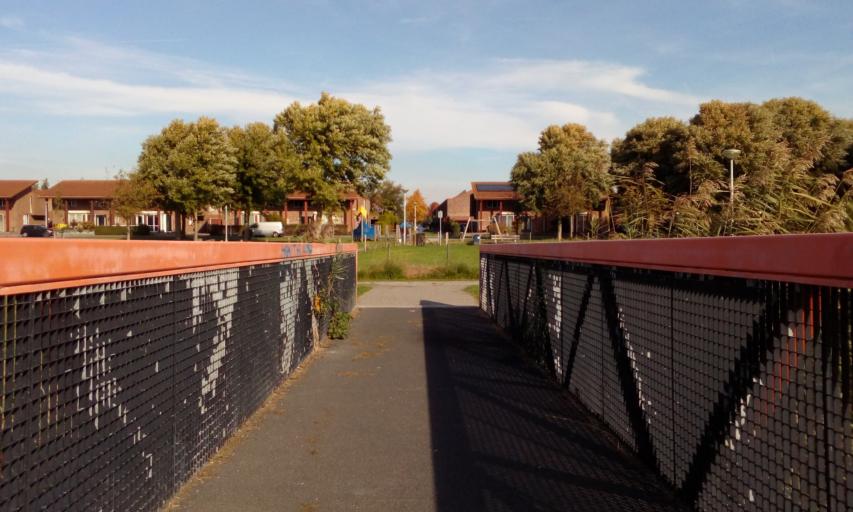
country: NL
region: Utrecht
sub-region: Stichtse Vecht
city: Spechtenkamp
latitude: 52.0785
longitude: 5.0100
